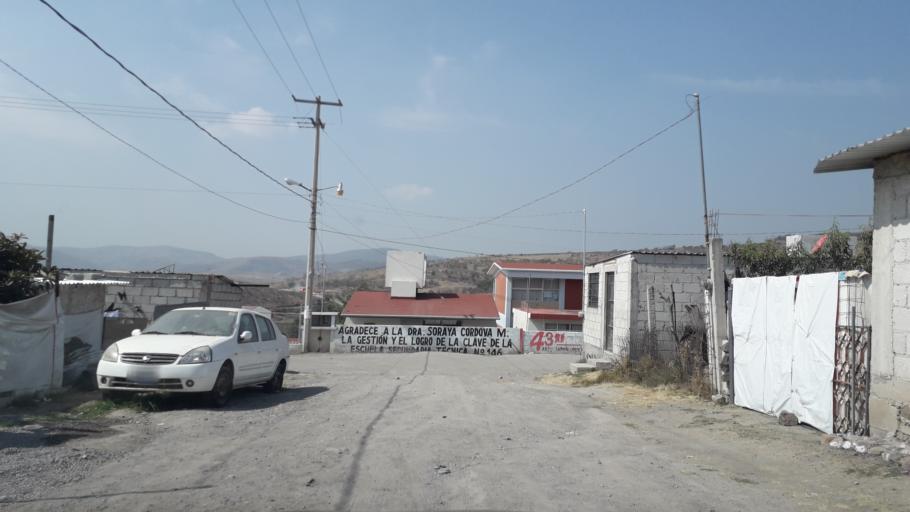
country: MX
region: Puebla
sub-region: Puebla
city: El Capulo (La Quebradora)
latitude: 18.9341
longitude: -98.2689
